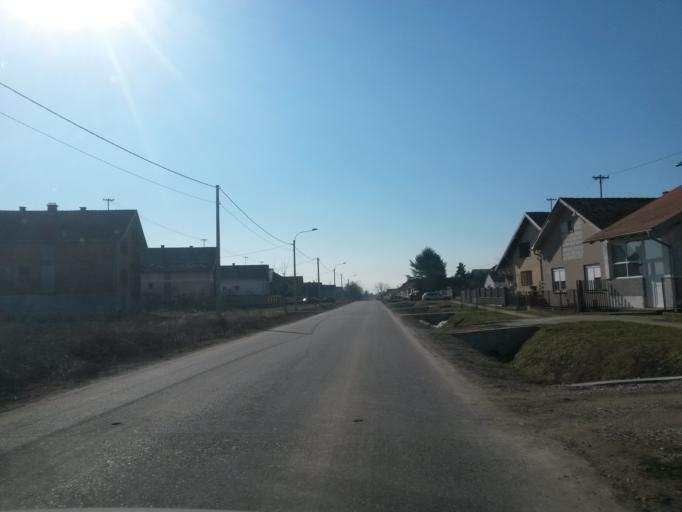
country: HR
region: Vukovarsko-Srijemska
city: Negoslavci
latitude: 45.2930
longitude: 19.0019
